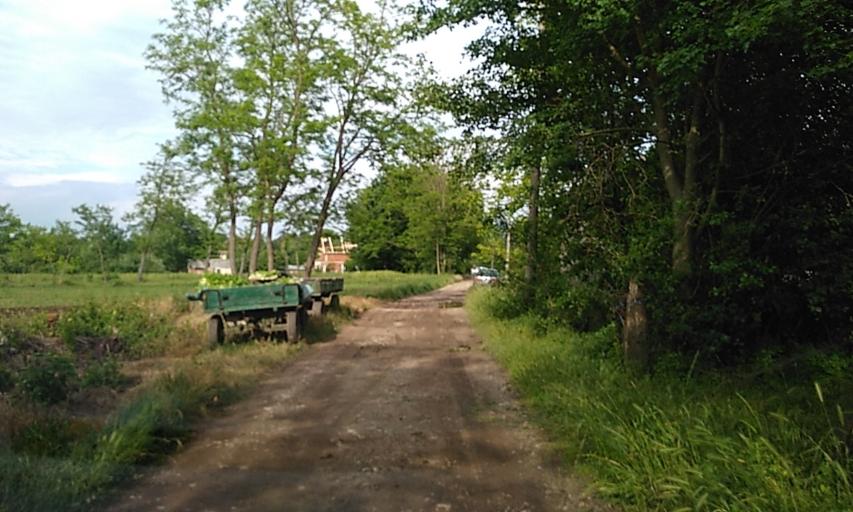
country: RS
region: Central Serbia
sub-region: Nisavski Okrug
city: Razanj
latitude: 43.5959
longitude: 21.6110
